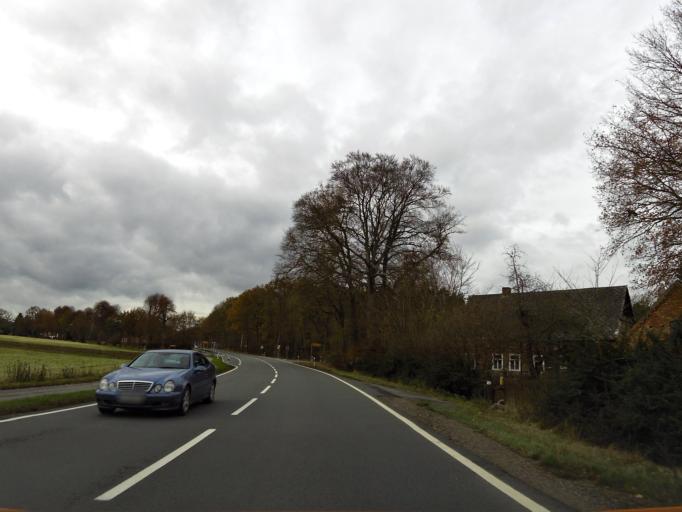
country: DE
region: Lower Saxony
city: Schnega
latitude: 52.9061
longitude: 10.9203
